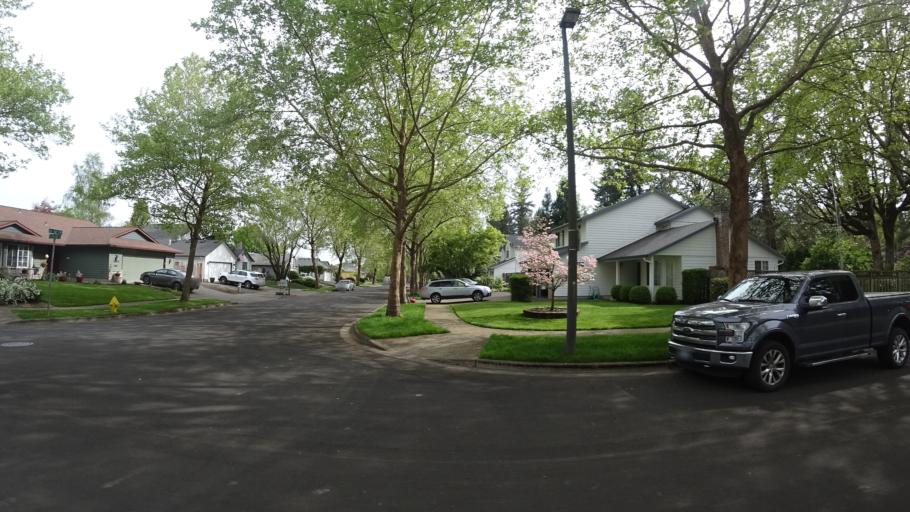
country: US
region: Oregon
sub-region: Washington County
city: Aloha
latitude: 45.5120
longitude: -122.9254
